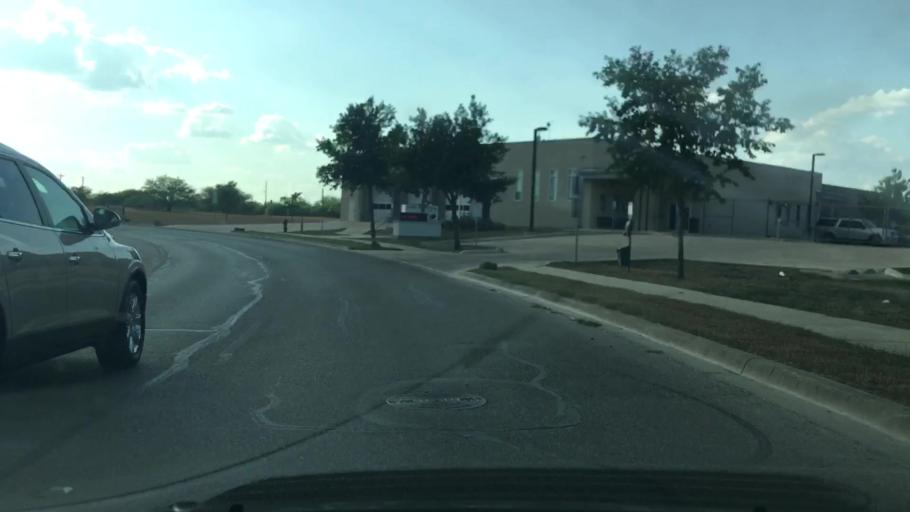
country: US
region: Texas
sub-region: Guadalupe County
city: Northcliff
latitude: 29.5945
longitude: -98.2517
